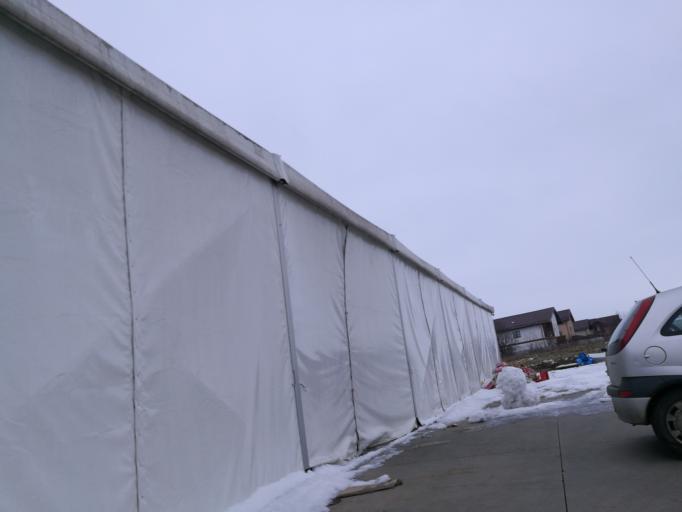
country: RO
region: Ilfov
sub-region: Comuna Tunari
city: Tunari
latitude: 44.5411
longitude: 26.1319
